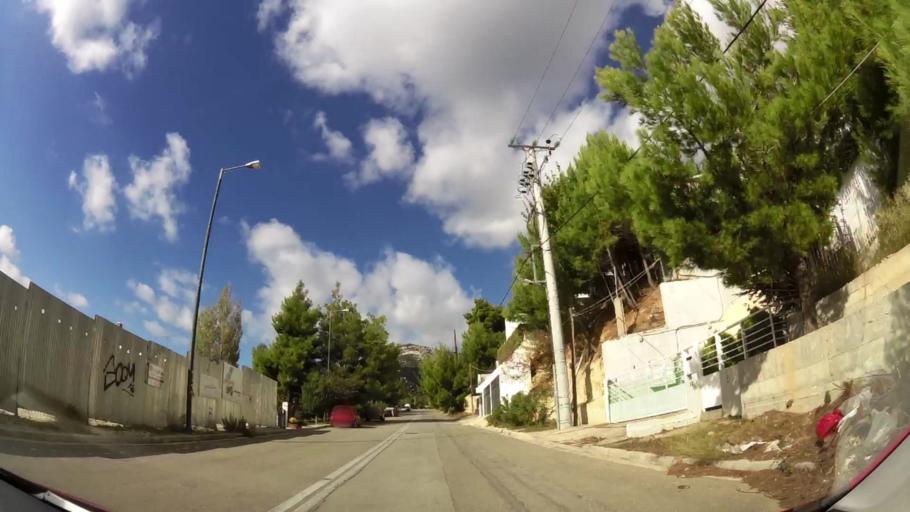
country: GR
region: Attica
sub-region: Nomarchia Anatolikis Attikis
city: Thrakomakedones
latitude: 38.1418
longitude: 23.7511
